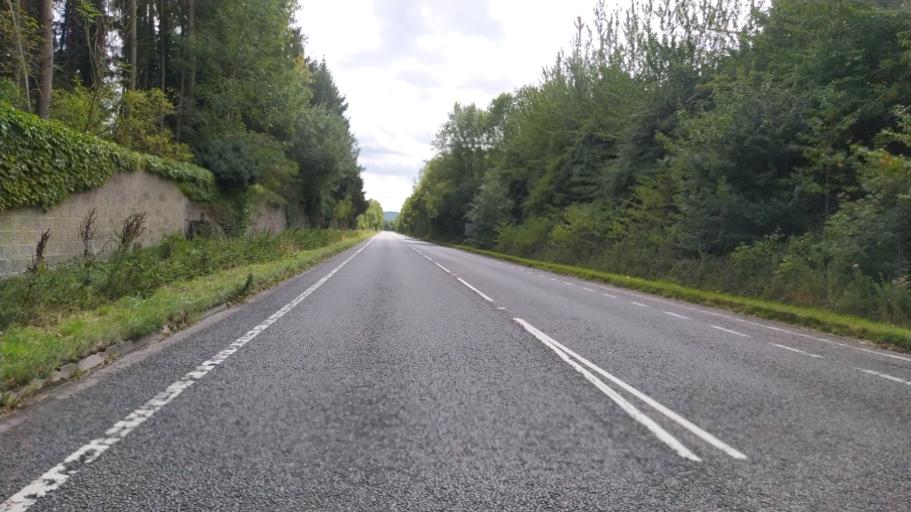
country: GB
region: England
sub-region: Wiltshire
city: Hindon
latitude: 51.0754
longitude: -2.1681
